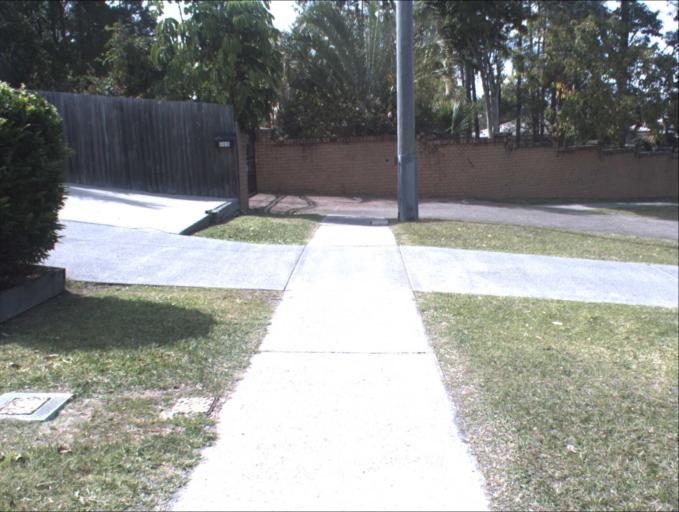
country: AU
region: Queensland
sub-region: Logan
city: Springwood
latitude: -27.6241
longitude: 153.1470
